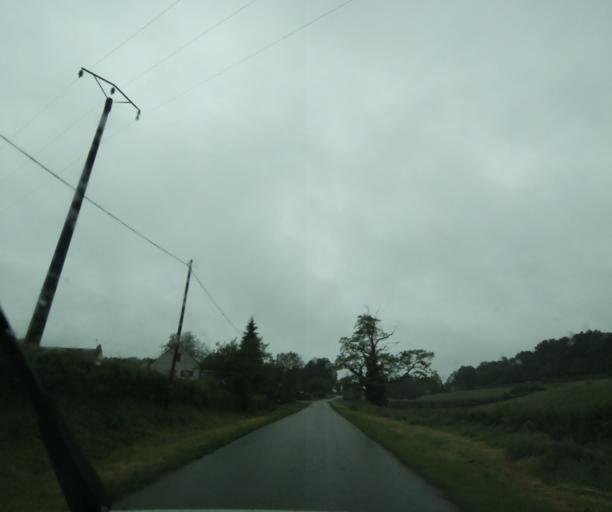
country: FR
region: Bourgogne
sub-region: Departement de Saone-et-Loire
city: Charolles
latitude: 46.4087
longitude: 4.2555
